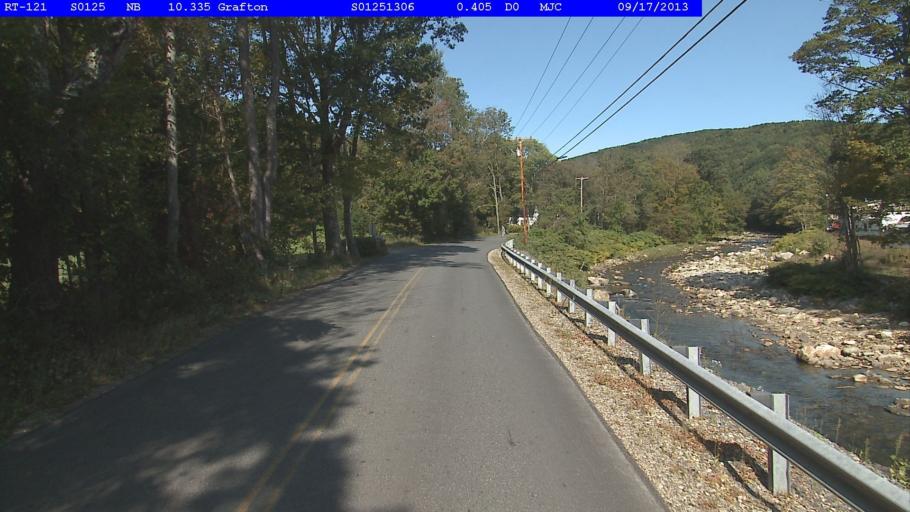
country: US
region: Vermont
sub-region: Windham County
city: Rockingham
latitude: 43.1525
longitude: -72.5628
